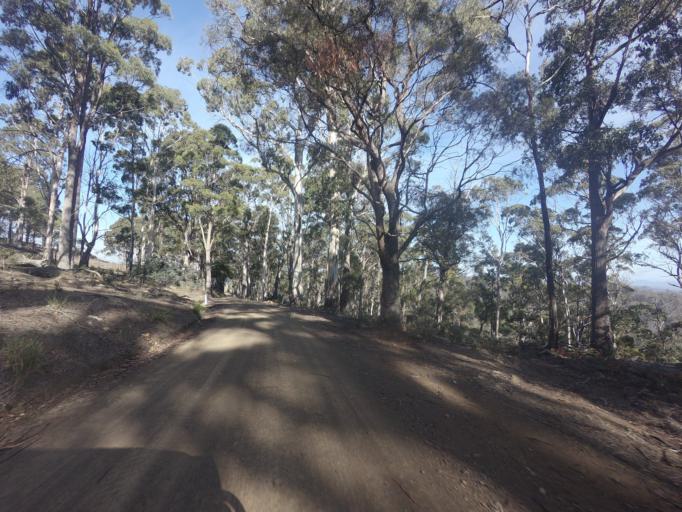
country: AU
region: Tasmania
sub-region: Sorell
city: Sorell
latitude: -42.5183
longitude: 147.4710
